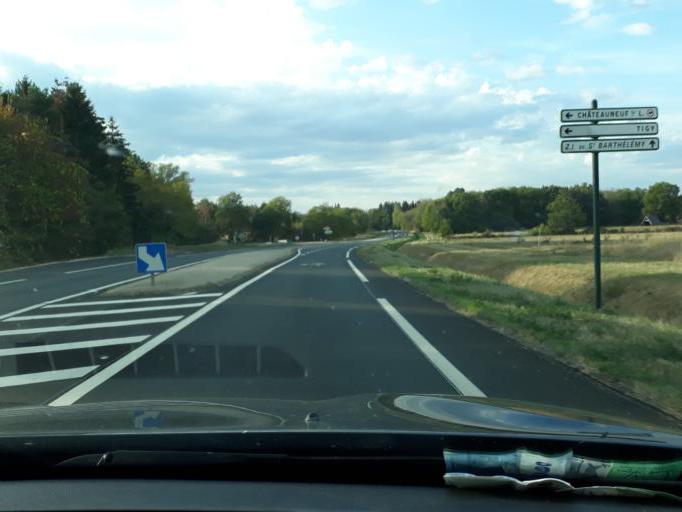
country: FR
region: Centre
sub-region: Departement du Loiret
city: Chateauneuf-sur-Loire
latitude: 47.8610
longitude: 2.2558
